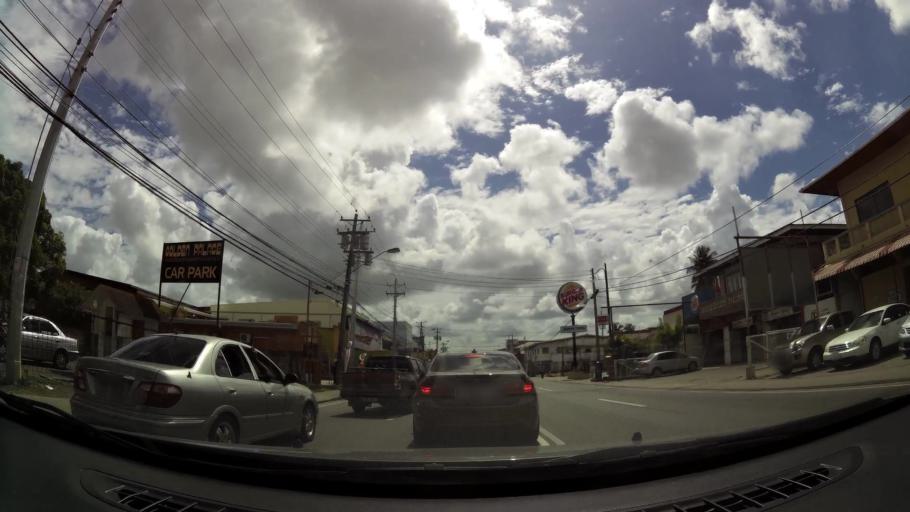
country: TT
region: City of San Fernando
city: Marabella
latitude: 10.3051
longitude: -61.4510
